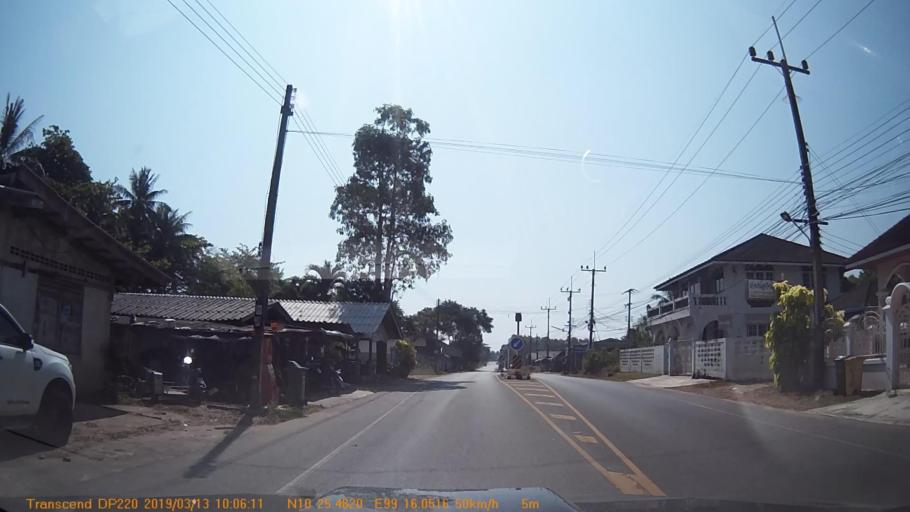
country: TH
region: Chumphon
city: Chumphon
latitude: 10.4246
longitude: 99.2678
